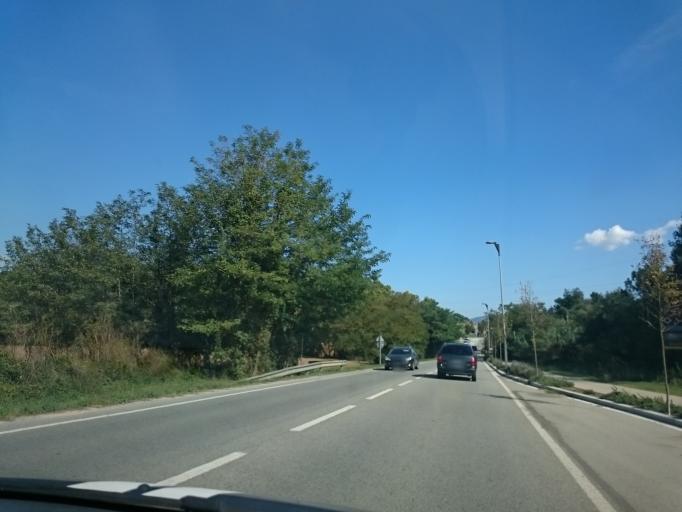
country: ES
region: Catalonia
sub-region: Provincia de Barcelona
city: Llinars del Valles
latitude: 41.6390
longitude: 2.3803
